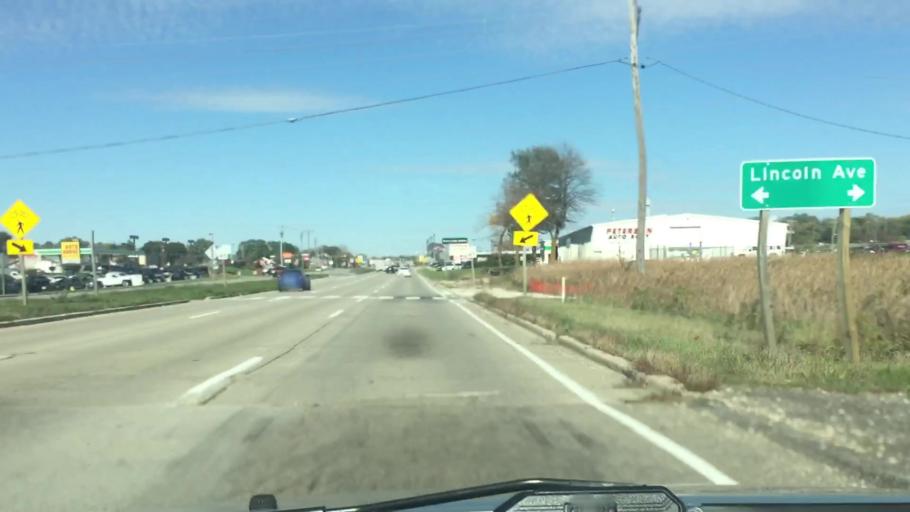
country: US
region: Wisconsin
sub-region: Waukesha County
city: Waukesha
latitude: 43.0098
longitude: -88.1998
